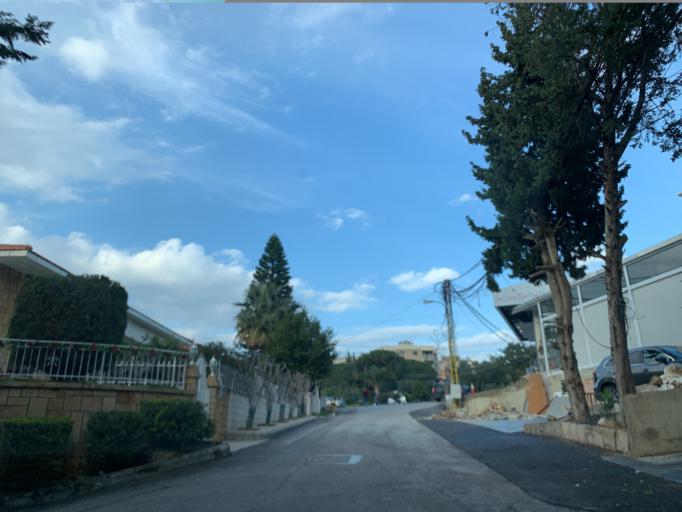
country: LB
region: Mont-Liban
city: Baabda
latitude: 33.8531
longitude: 35.5774
